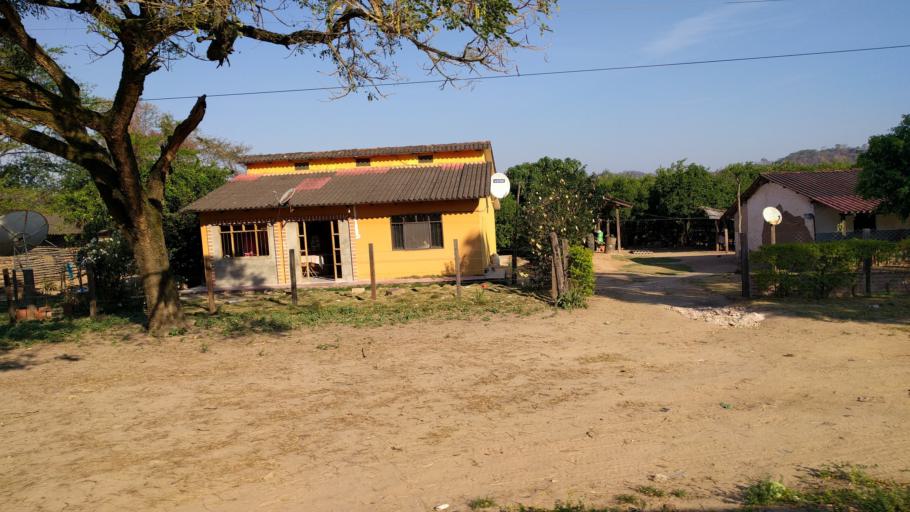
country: BO
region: Santa Cruz
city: Jorochito
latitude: -18.1442
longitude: -63.4818
